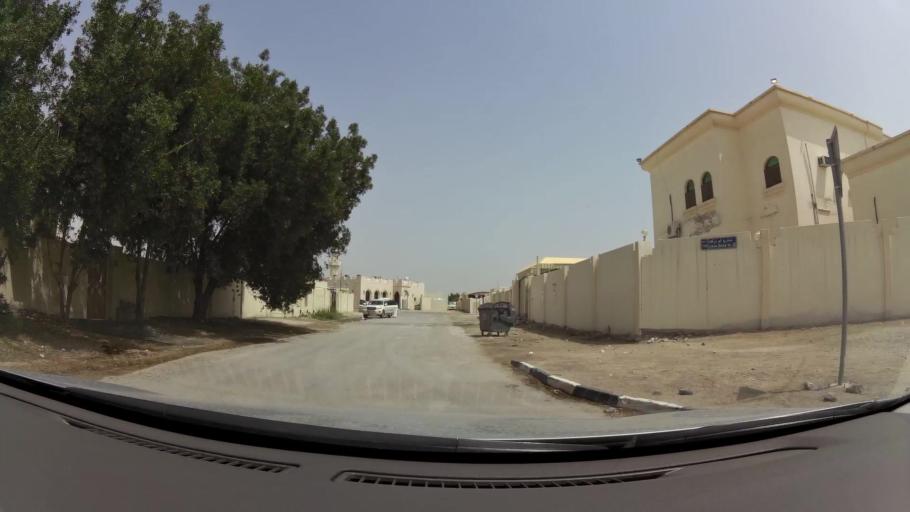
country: QA
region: Baladiyat ar Rayyan
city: Ar Rayyan
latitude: 25.2318
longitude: 51.4167
